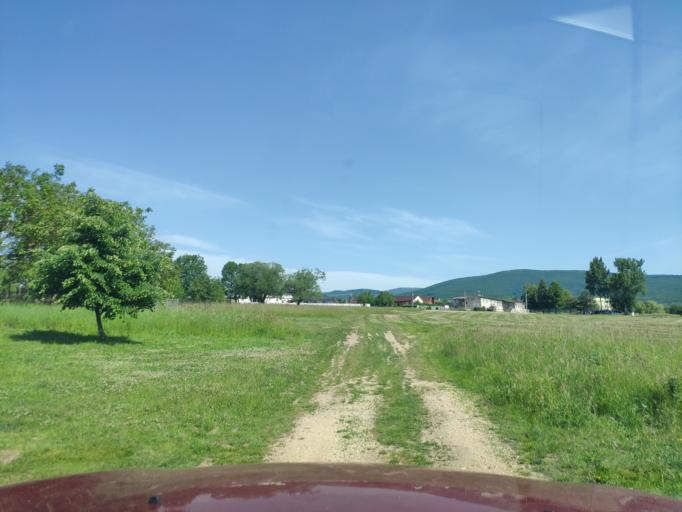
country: SK
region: Kosicky
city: Moldava nad Bodvou
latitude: 48.6912
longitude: 21.0118
